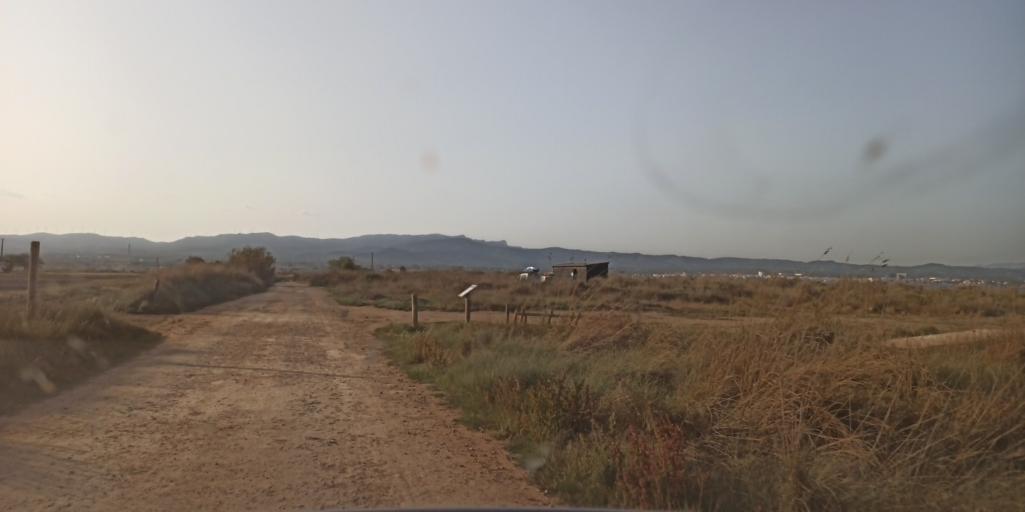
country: ES
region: Catalonia
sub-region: Provincia de Tarragona
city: L'Ampolla
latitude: 40.7809
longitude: 0.7150
